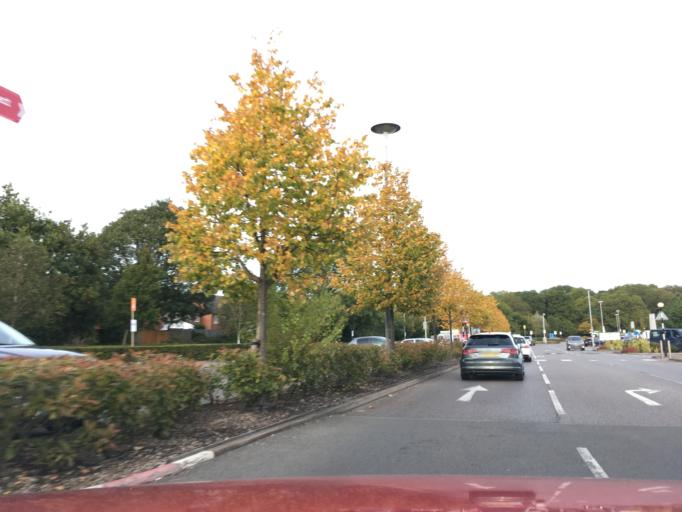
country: GB
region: England
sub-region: South Gloucestershire
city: Stoke Gifford
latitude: 51.5369
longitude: -2.5515
